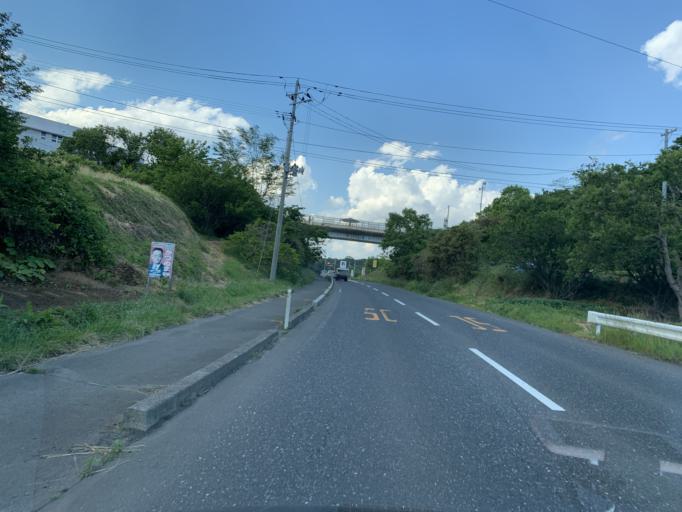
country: JP
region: Miyagi
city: Wakuya
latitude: 38.5383
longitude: 141.1501
